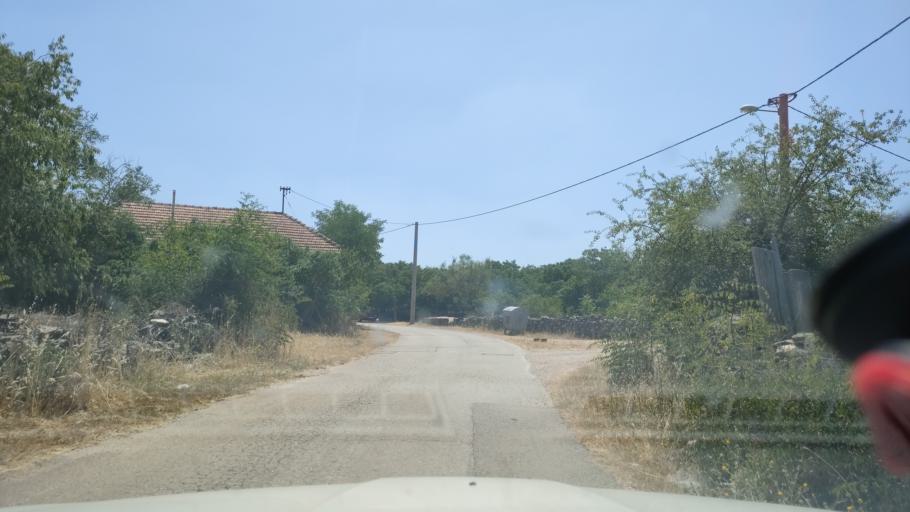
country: HR
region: Sibensko-Kniniska
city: Kistanje
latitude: 43.9572
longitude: 15.8771
